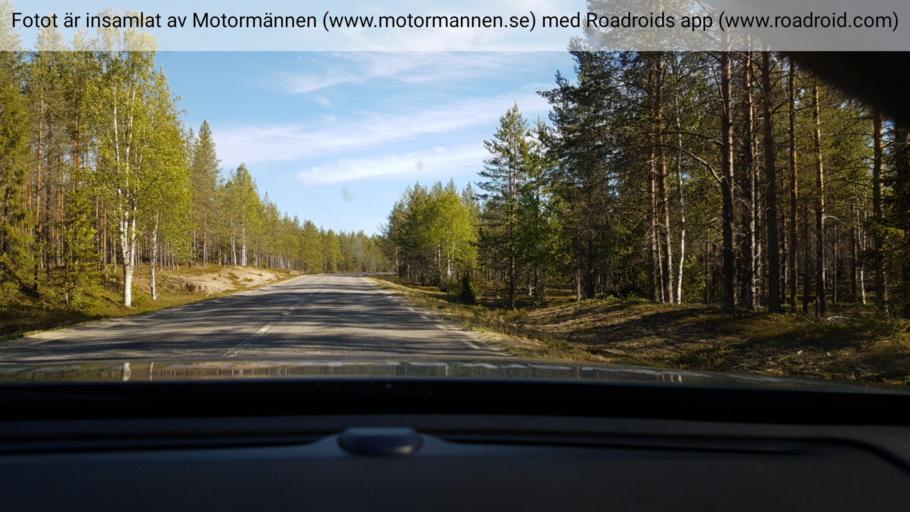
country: SE
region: Vaesterbotten
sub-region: Norsjo Kommun
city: Norsjoe
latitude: 64.7353
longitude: 19.1283
